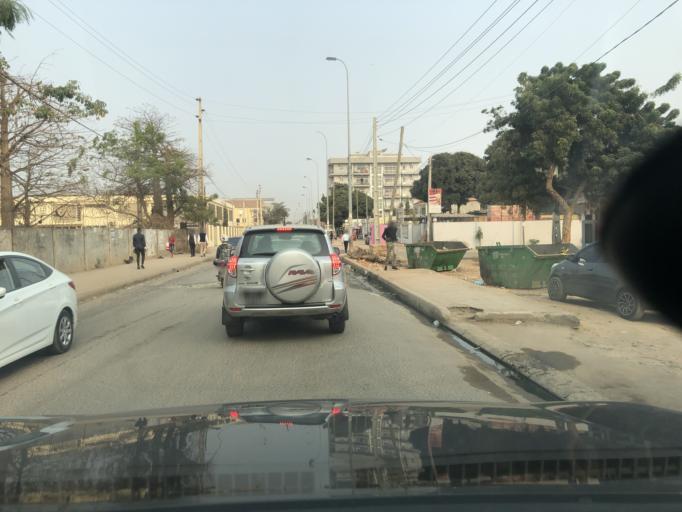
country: AO
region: Luanda
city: Luanda
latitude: -8.8815
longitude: 13.1983
